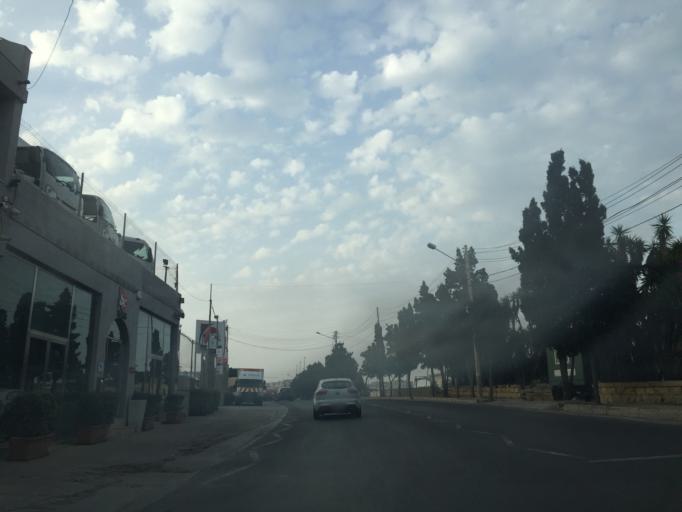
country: MT
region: Saint Paul's Bay
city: San Pawl il-Bahar
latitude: 35.9399
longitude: 14.4114
